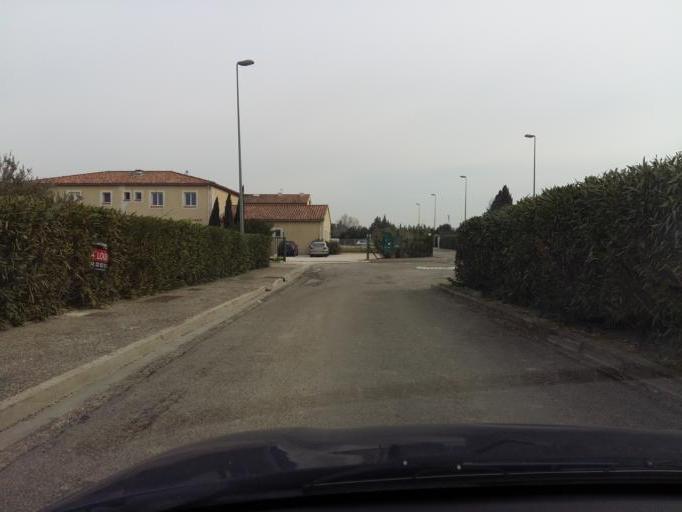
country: FR
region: Provence-Alpes-Cote d'Azur
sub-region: Departement des Bouches-du-Rhone
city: Chateaurenard
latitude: 43.8854
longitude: 4.8681
